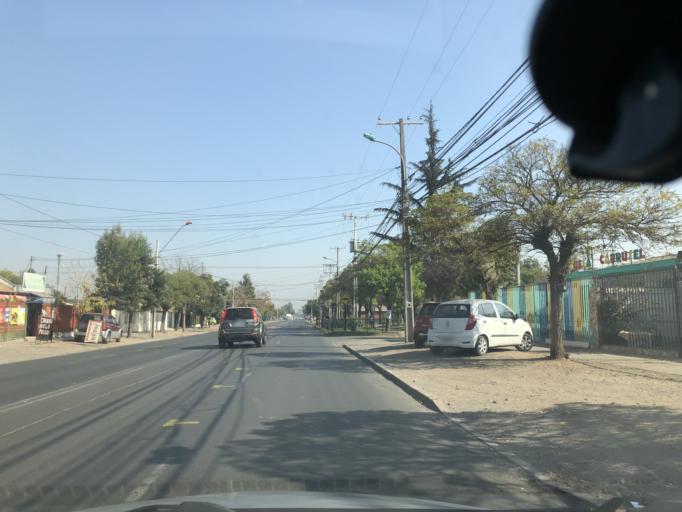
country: CL
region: Santiago Metropolitan
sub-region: Provincia de Cordillera
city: Puente Alto
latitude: -33.6046
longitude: -70.5669
